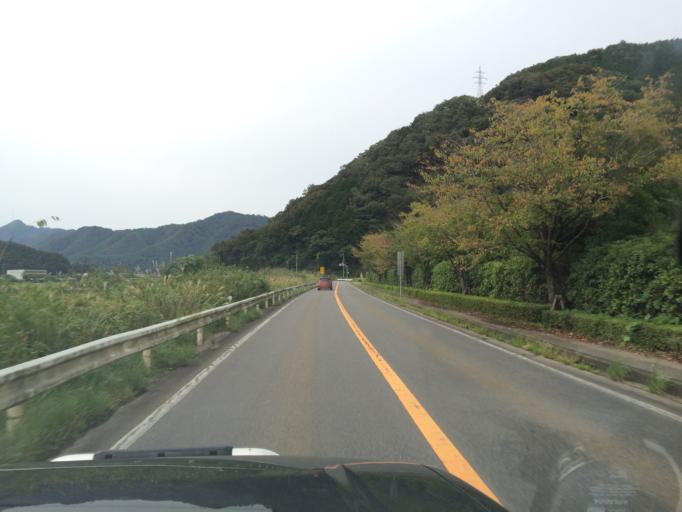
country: JP
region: Hyogo
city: Toyooka
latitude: 35.3945
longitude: 134.7928
